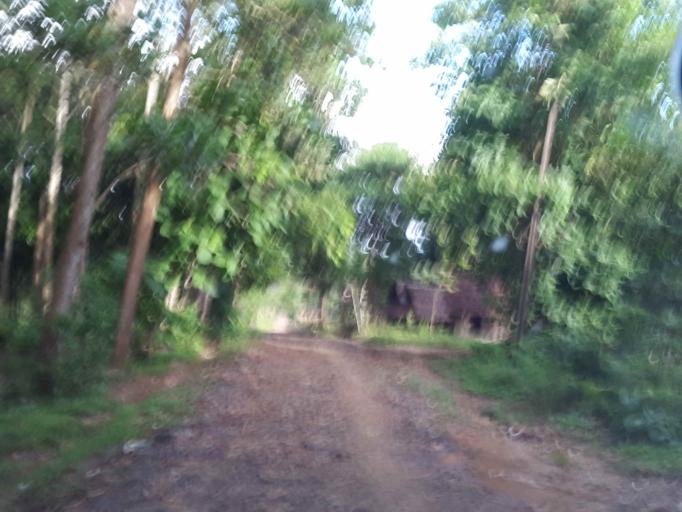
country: ID
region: Banten
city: Cibaliung
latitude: -6.7059
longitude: 105.7229
